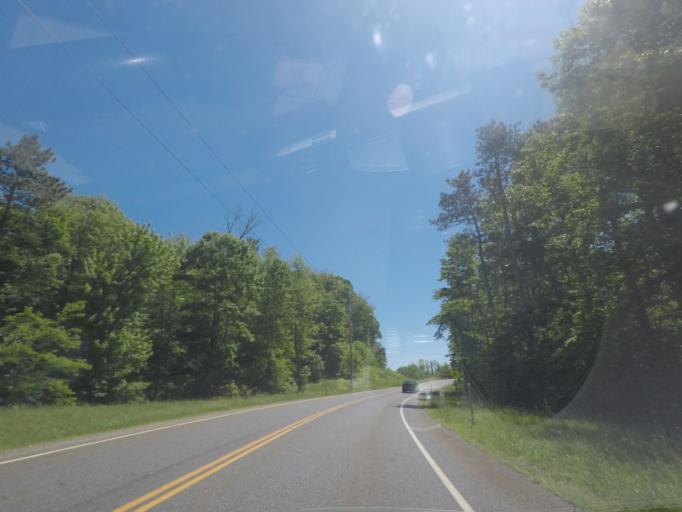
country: US
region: New York
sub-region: Saratoga County
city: Mechanicville
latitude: 42.9472
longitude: -73.7216
